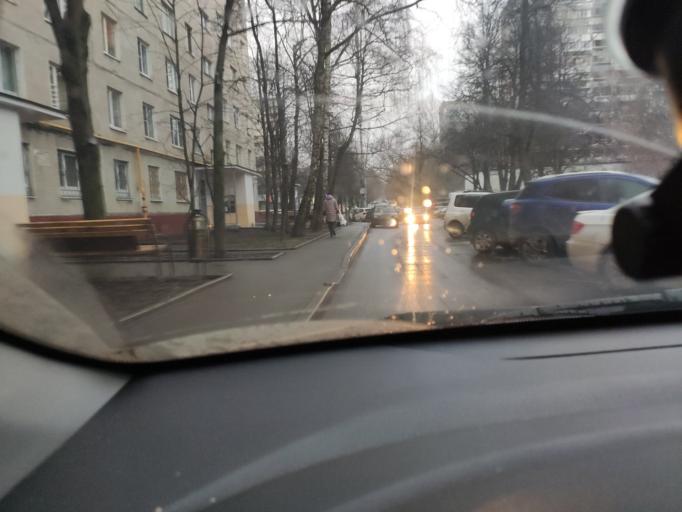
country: RU
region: Moscow
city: Chertanovo Yuzhnoye
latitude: 55.6033
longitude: 37.5923
